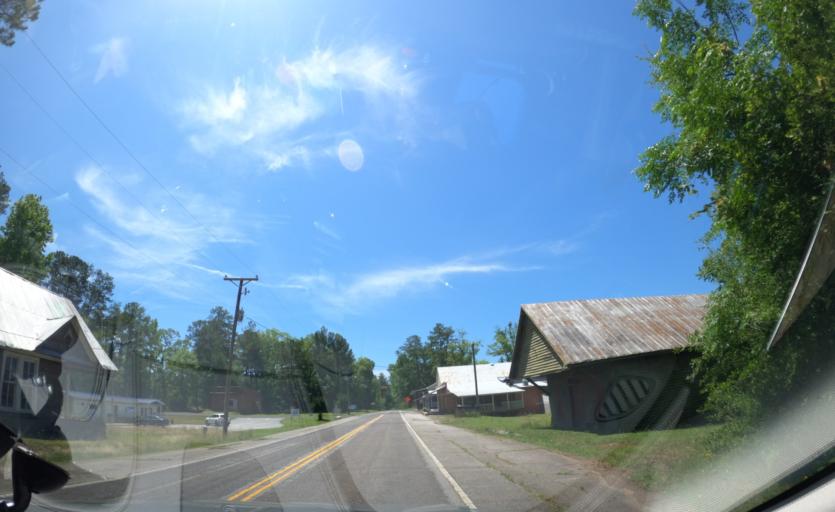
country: US
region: South Carolina
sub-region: Abbeville County
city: Calhoun Falls
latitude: 34.0080
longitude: -82.5072
